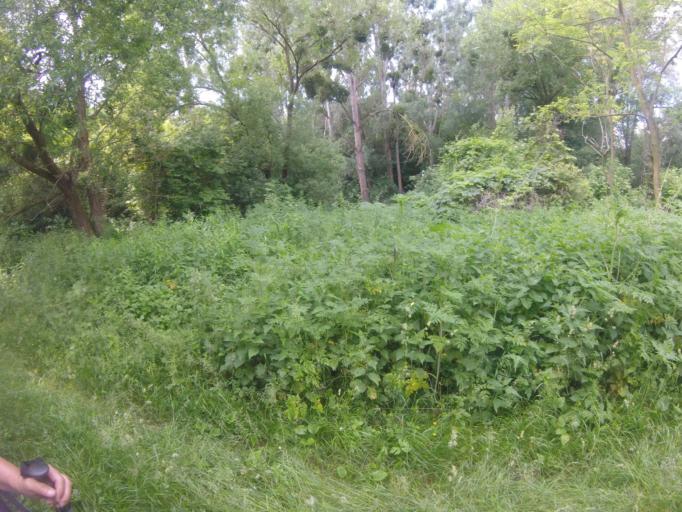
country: HU
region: Veszprem
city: Cseteny
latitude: 47.2815
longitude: 18.0261
